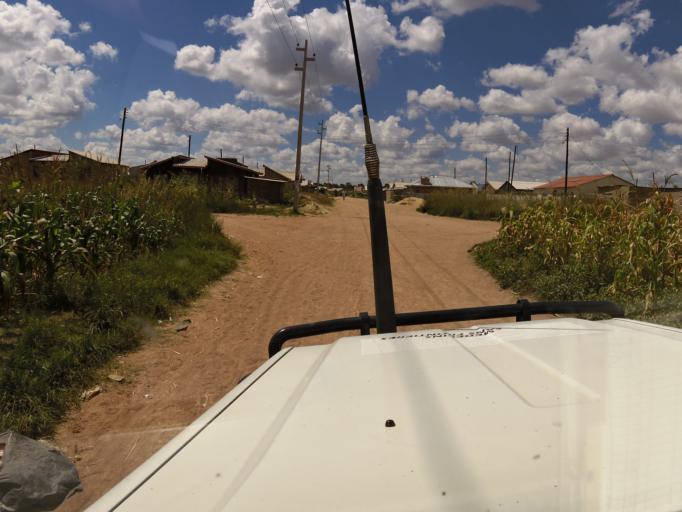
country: ZW
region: Harare
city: Epworth
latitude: -17.9218
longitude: 31.1417
